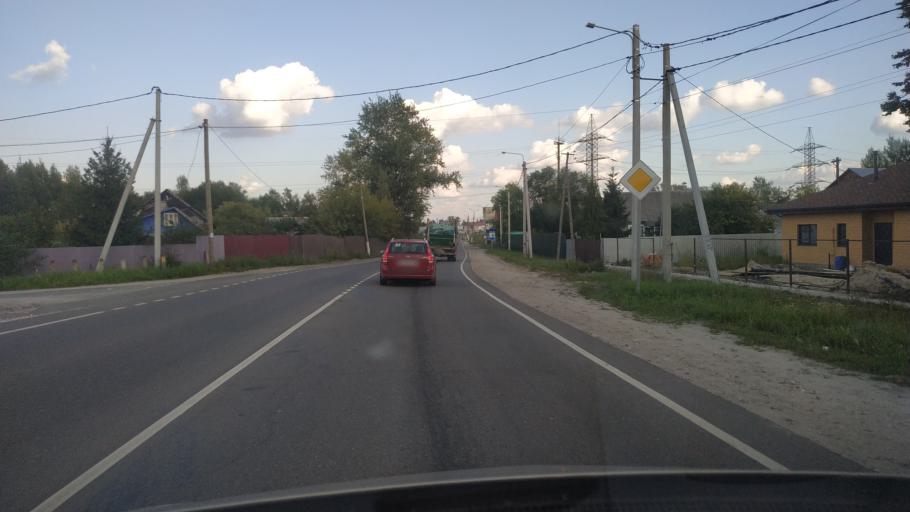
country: RU
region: Moskovskaya
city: Shatura
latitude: 55.5765
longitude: 39.4977
